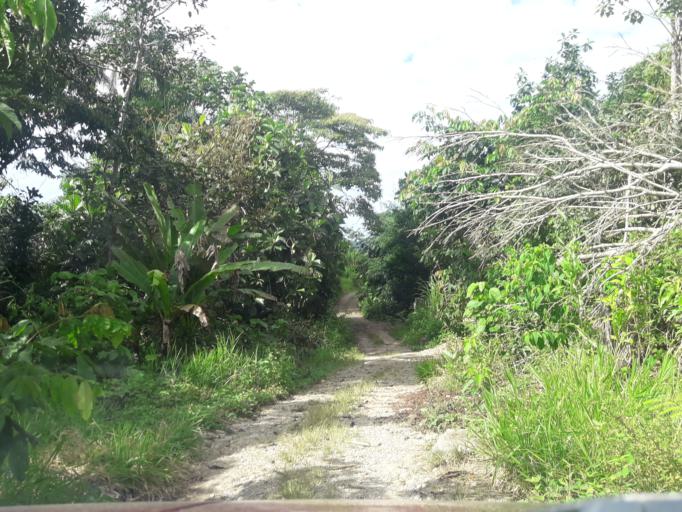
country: EC
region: Napo
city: Tena
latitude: -0.9821
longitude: -77.8185
